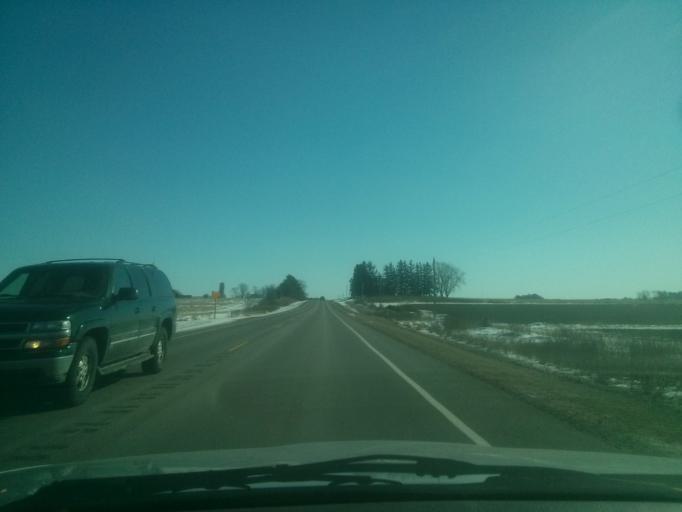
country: US
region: Wisconsin
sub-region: Polk County
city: Clear Lake
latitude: 45.1364
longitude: -92.3437
